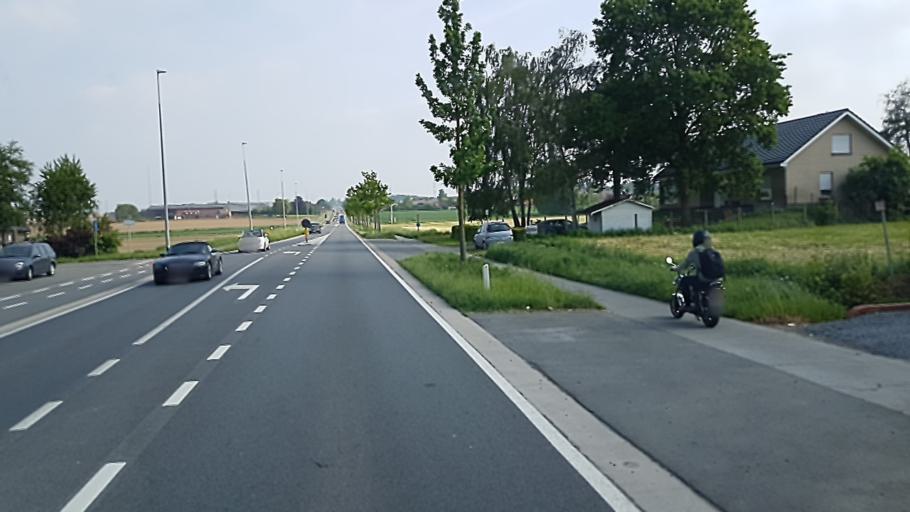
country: BE
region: Flanders
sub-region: Provincie West-Vlaanderen
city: Kortrijk
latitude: 50.7899
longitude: 3.2933
